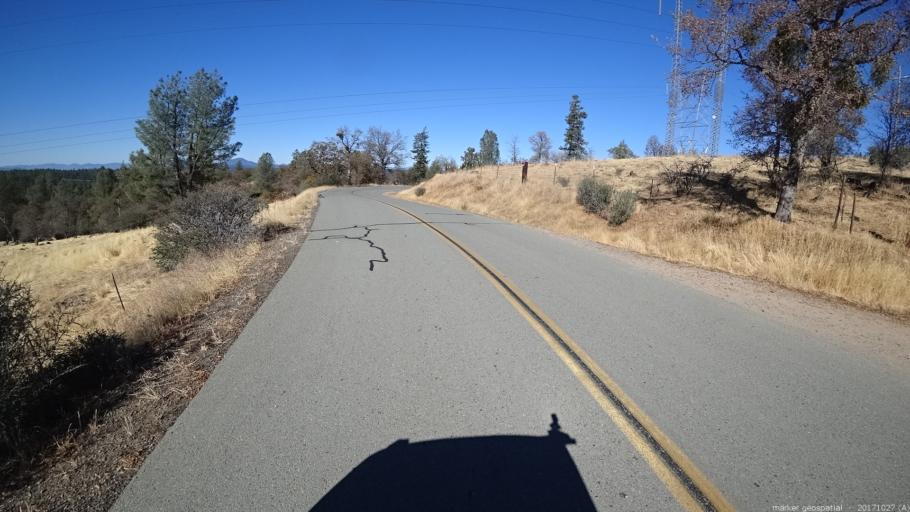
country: US
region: California
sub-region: Shasta County
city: Shingletown
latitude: 40.7569
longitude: -121.9672
